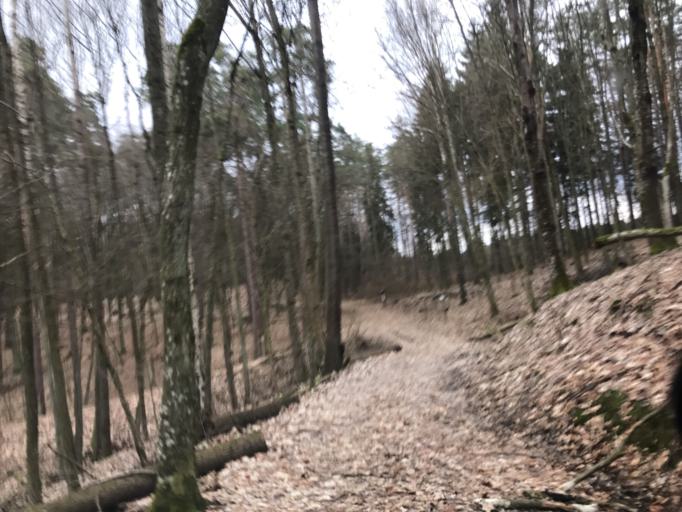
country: PL
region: Kujawsko-Pomorskie
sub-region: Powiat brodnicki
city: Gorzno
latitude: 53.1836
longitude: 19.6588
